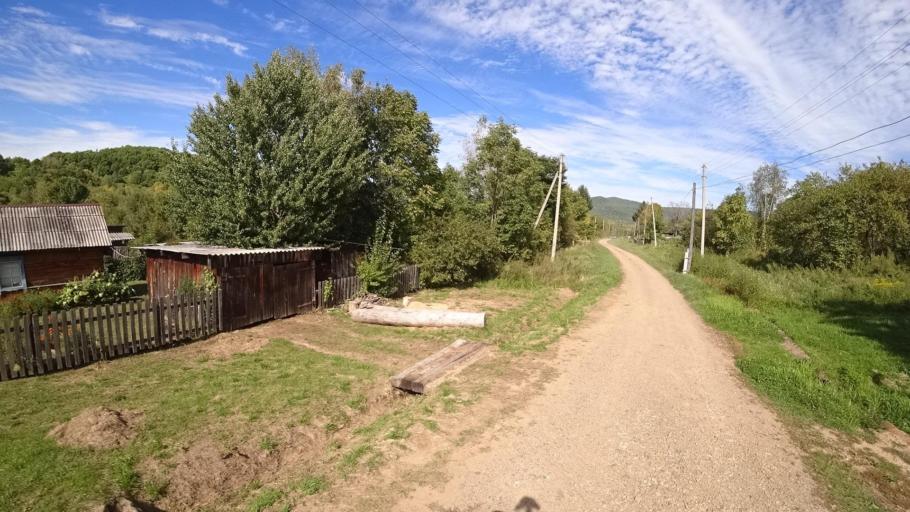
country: RU
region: Primorskiy
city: Yakovlevka
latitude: 44.3873
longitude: 133.6007
